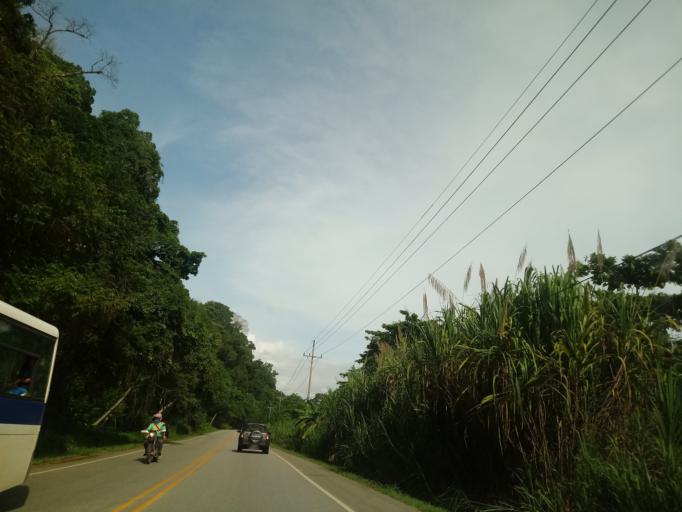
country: CR
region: San Jose
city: Daniel Flores
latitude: 9.1961
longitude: -83.7825
